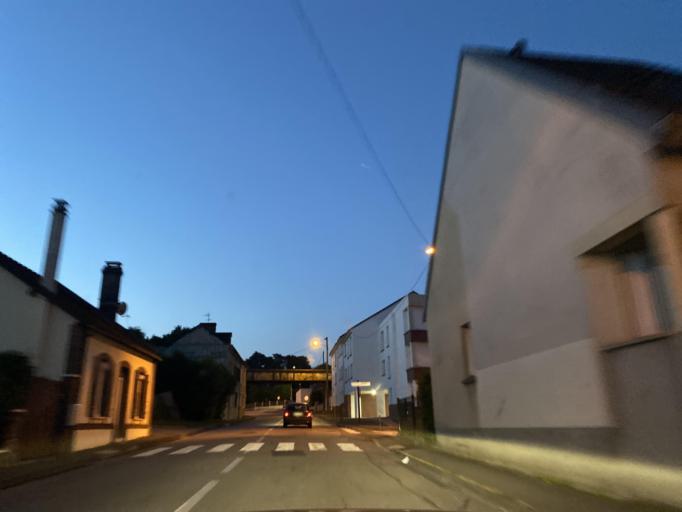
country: FR
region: Haute-Normandie
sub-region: Departement de l'Eure
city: Evreux
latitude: 49.0309
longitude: 1.1602
